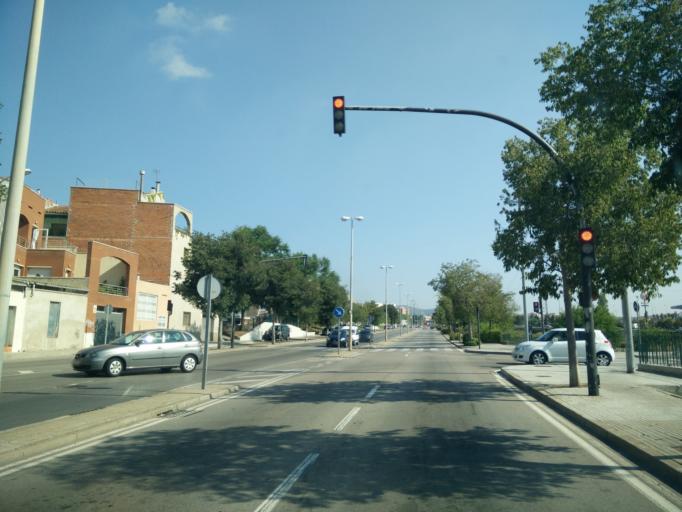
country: ES
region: Catalonia
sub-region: Provincia de Barcelona
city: Terrassa
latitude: 41.5616
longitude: 2.0329
